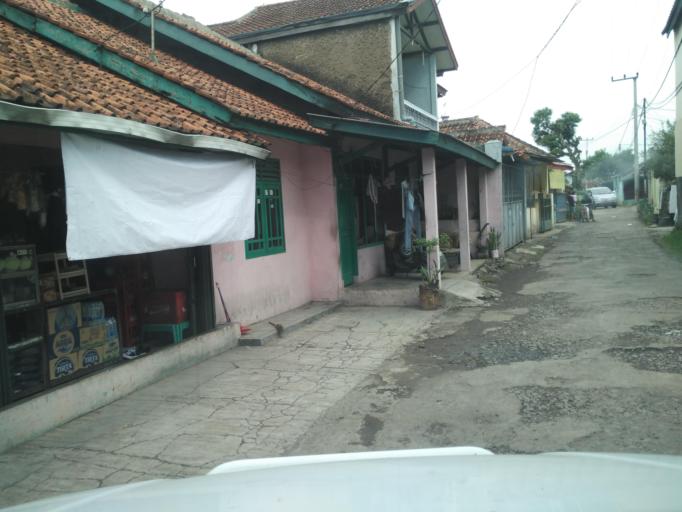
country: ID
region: West Java
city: Ciranjang-hilir
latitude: -6.8085
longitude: 107.1542
